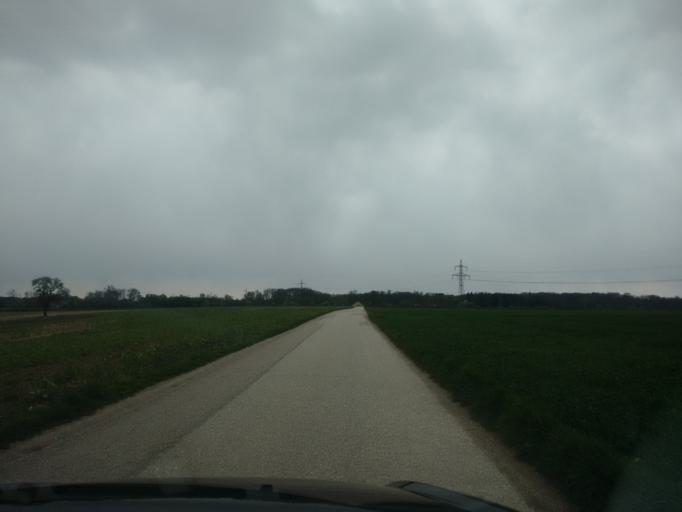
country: AT
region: Upper Austria
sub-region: Wels-Land
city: Holzhausen
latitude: 48.2081
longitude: 14.0815
